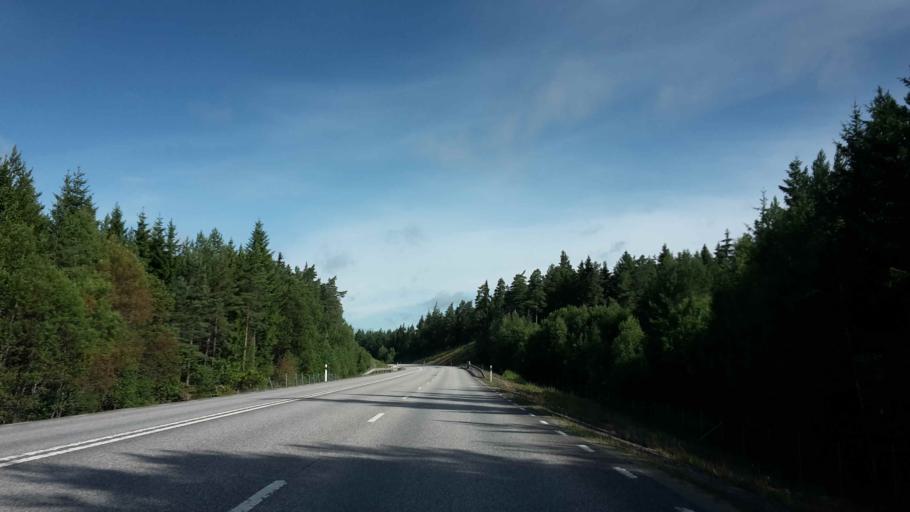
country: SE
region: OEstergoetland
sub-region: Motala Kommun
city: Borensberg
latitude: 58.5670
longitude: 15.3031
